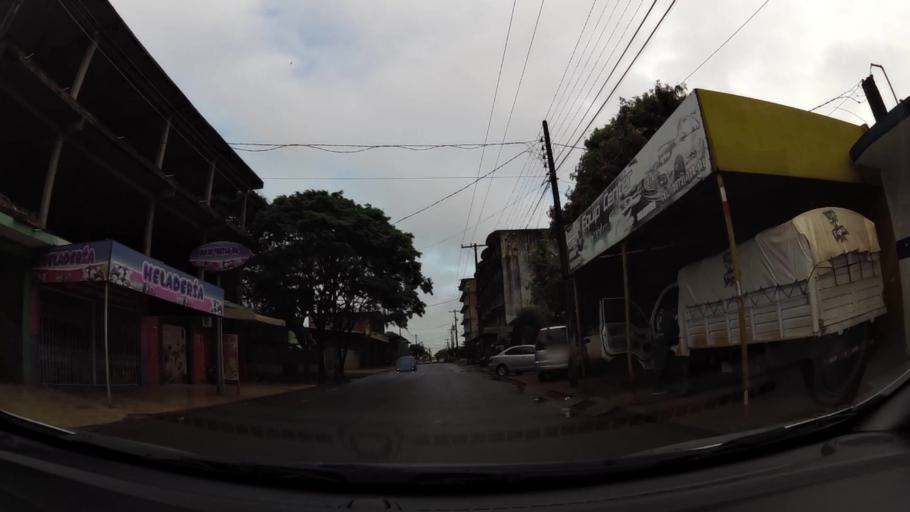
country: PY
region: Alto Parana
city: Presidente Franco
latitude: -25.5182
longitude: -54.6713
